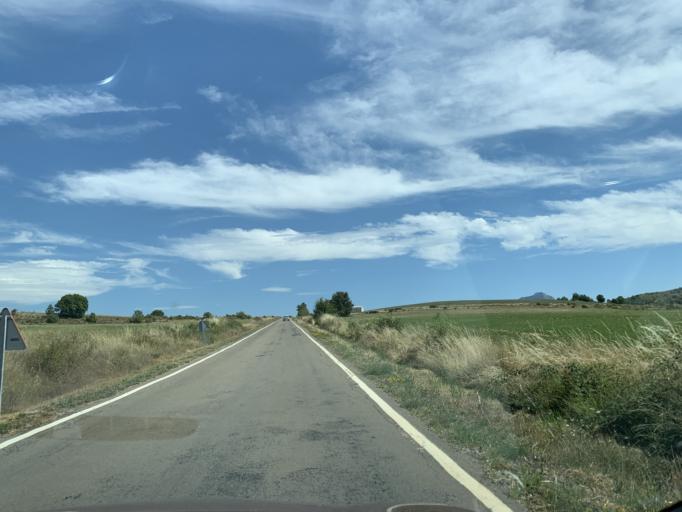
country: ES
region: Aragon
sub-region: Provincia de Huesca
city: Santa Cruz de la Seros
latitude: 42.5978
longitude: -0.6555
